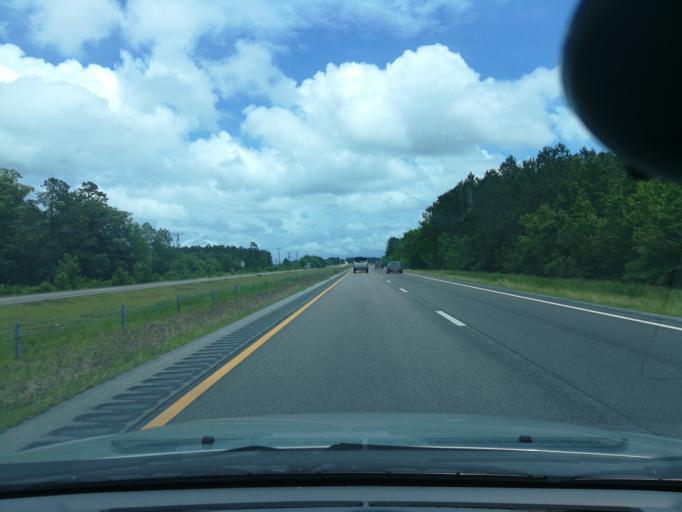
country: US
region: North Carolina
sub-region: Tyrrell County
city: Columbia
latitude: 35.9021
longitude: -76.3287
